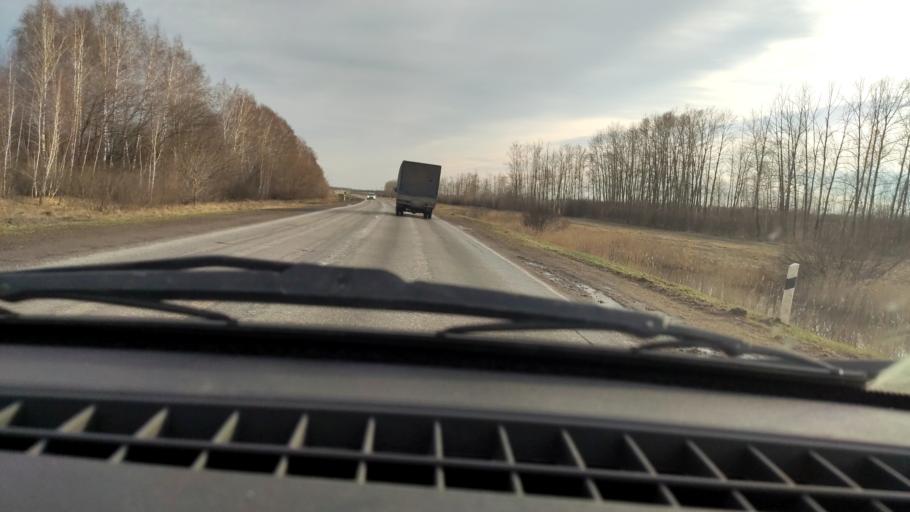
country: RU
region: Bashkortostan
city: Davlekanovo
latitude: 54.3491
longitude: 55.1778
